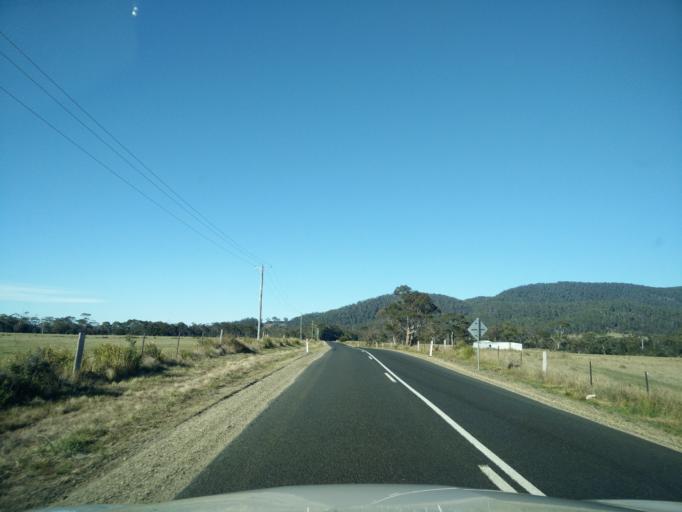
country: AU
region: Tasmania
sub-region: Break O'Day
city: St Helens
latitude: -41.8919
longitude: 148.2661
